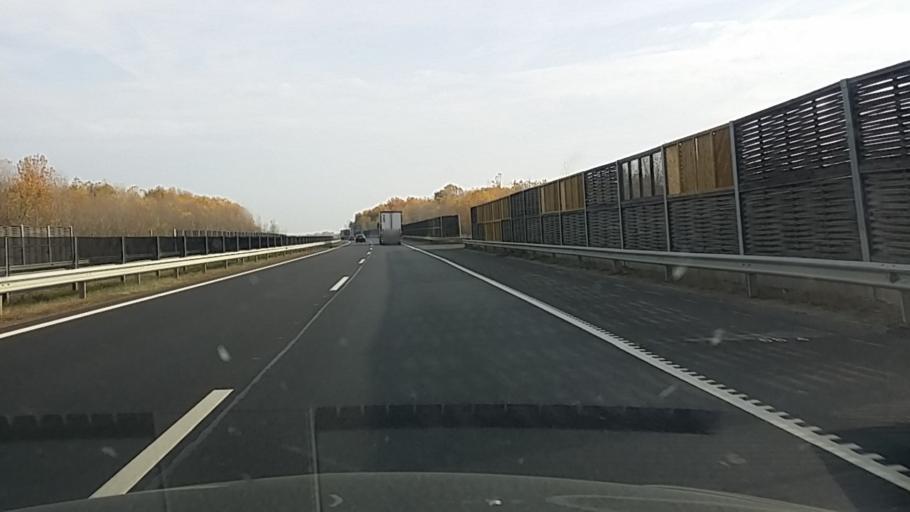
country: HU
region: Hajdu-Bihar
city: Polgar
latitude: 47.8521
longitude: 21.0599
